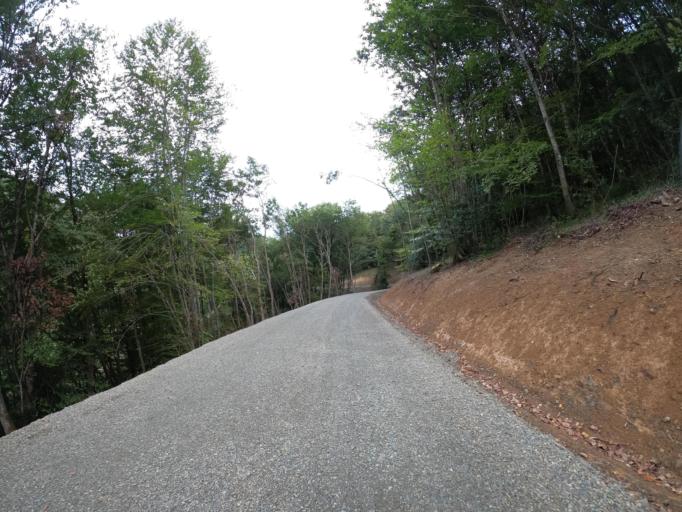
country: ES
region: Navarre
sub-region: Provincia de Navarra
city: Lekunberri
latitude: 43.0181
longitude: -1.9003
